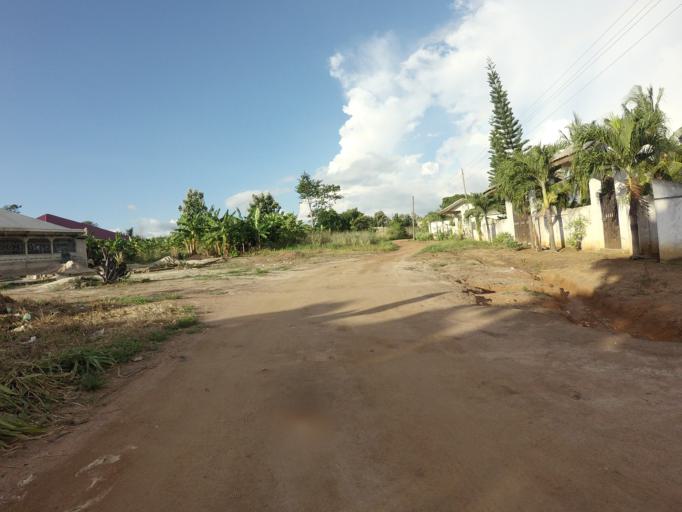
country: GH
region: Ashanti
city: Tafo
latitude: 6.9215
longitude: -1.6649
